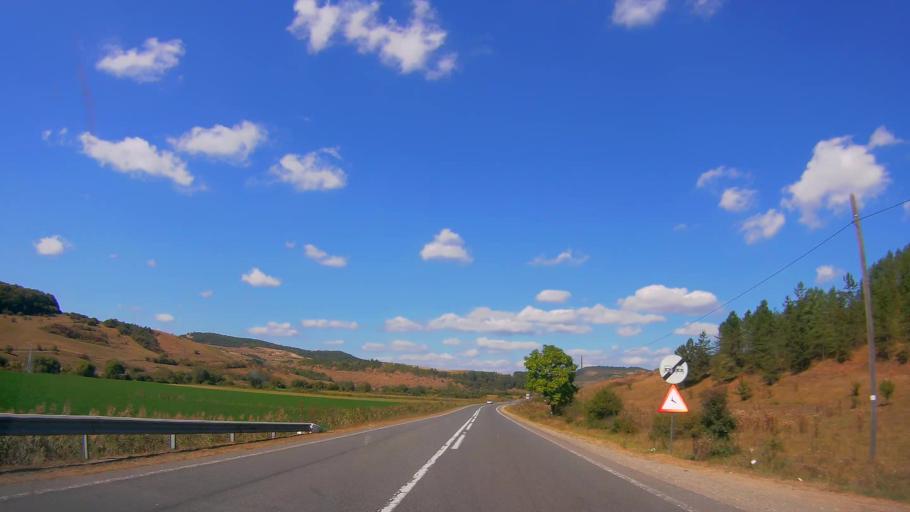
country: RO
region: Cluj
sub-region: Comuna Sanpaul
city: Sanpaul
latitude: 46.8376
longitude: 23.4069
